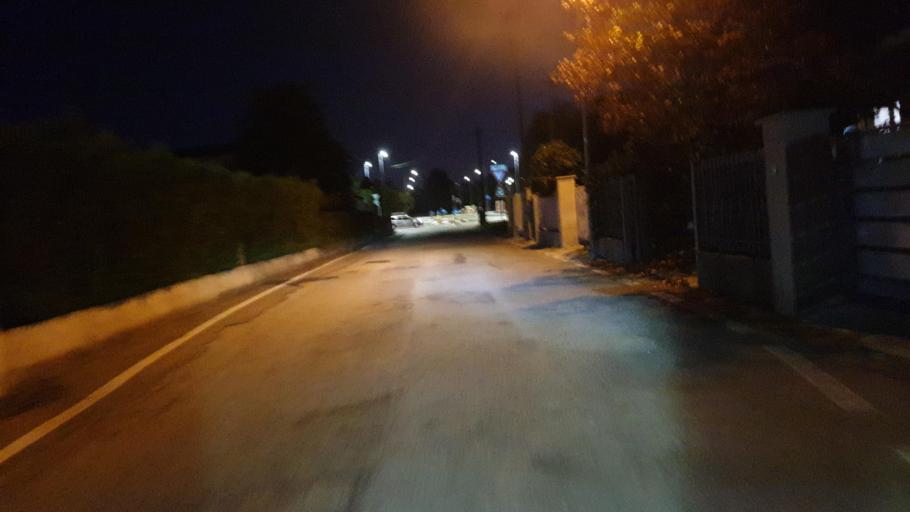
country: IT
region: Veneto
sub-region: Provincia di Venezia
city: Tombelle
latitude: 45.3970
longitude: 11.9771
